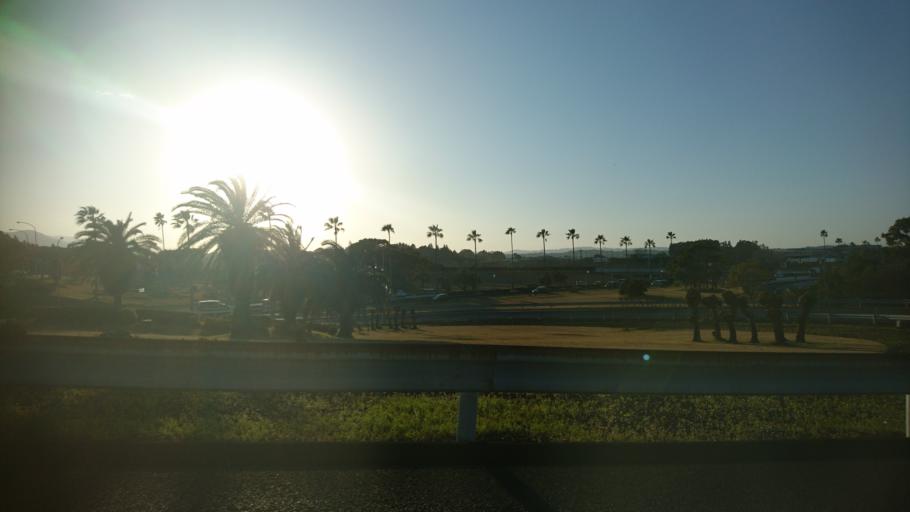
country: JP
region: Miyazaki
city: Miyazaki-shi
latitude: 31.8711
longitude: 131.4166
